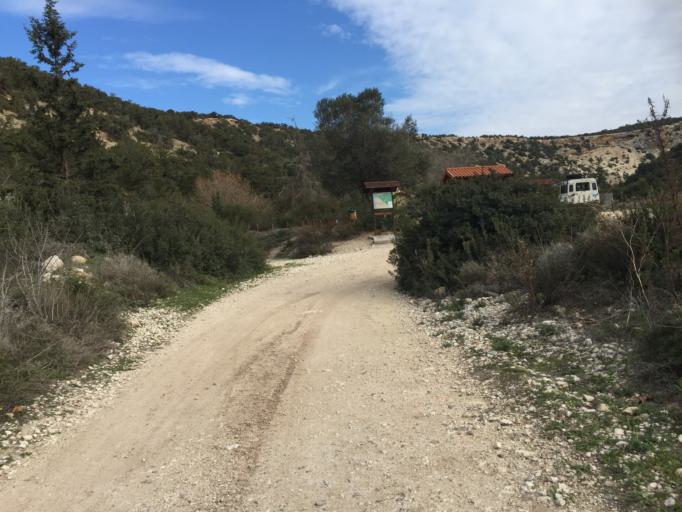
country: CY
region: Pafos
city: Pegeia
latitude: 34.9203
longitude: 32.3377
